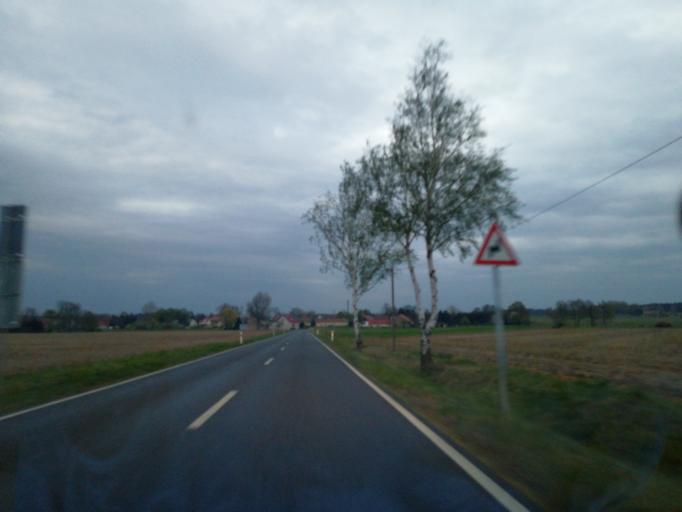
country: DE
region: Brandenburg
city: Calau
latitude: 51.7649
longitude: 13.9061
